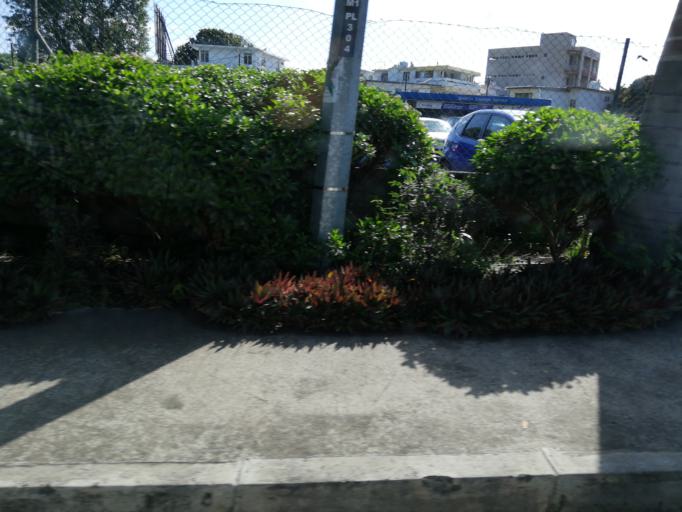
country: MU
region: Port Louis
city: Port Louis
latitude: -20.1633
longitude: 57.4928
